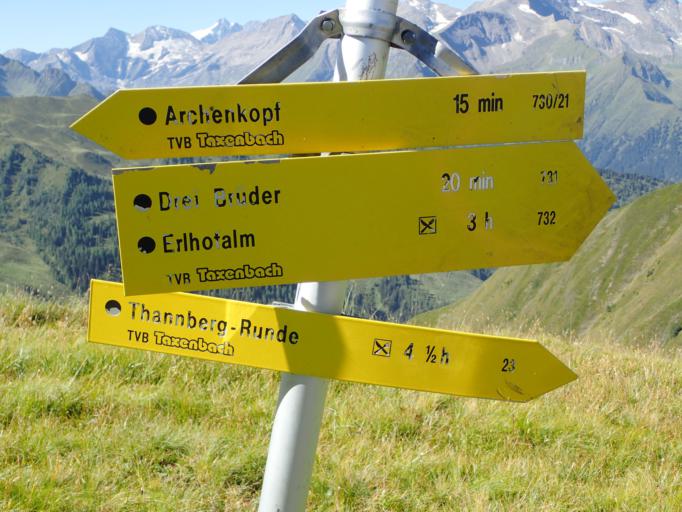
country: AT
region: Salzburg
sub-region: Politischer Bezirk Zell am See
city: Bruck an der Grossglocknerstrasse
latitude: 47.2406
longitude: 12.8909
